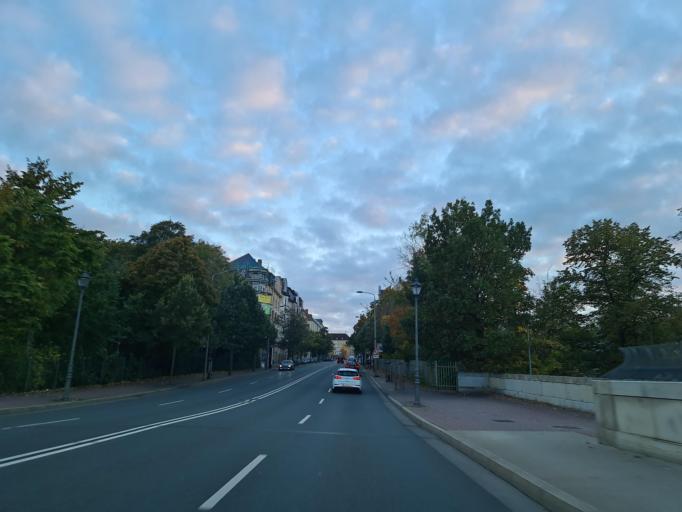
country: DE
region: Saxony
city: Plauen
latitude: 50.4986
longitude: 12.1261
